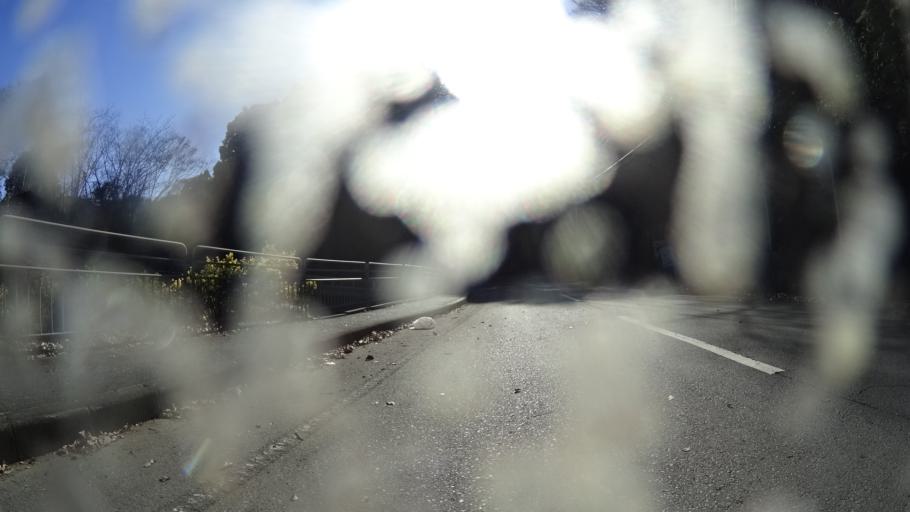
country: JP
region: Yamanashi
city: Uenohara
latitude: 35.6243
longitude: 139.1512
